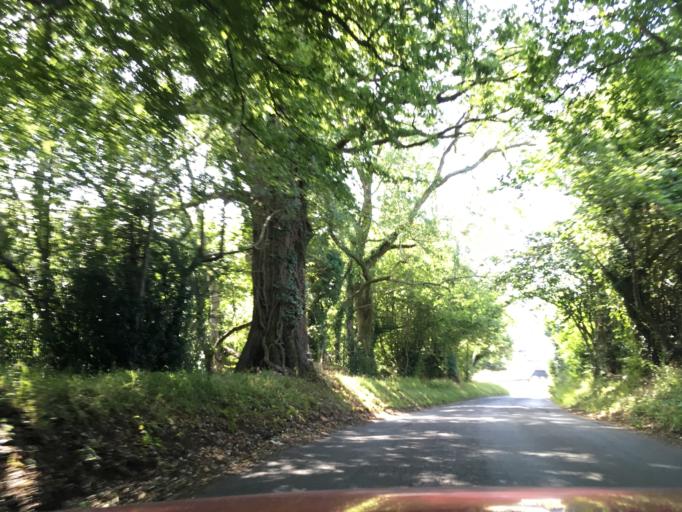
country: GB
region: England
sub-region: West Berkshire
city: Kintbury
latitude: 51.3808
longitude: -1.4481
